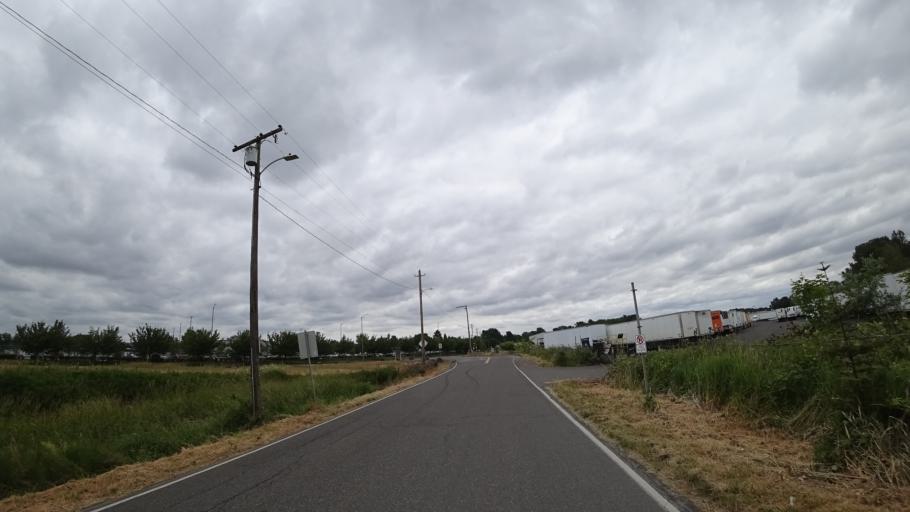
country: US
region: Washington
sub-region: Clark County
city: Vancouver
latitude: 45.5906
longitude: -122.6574
